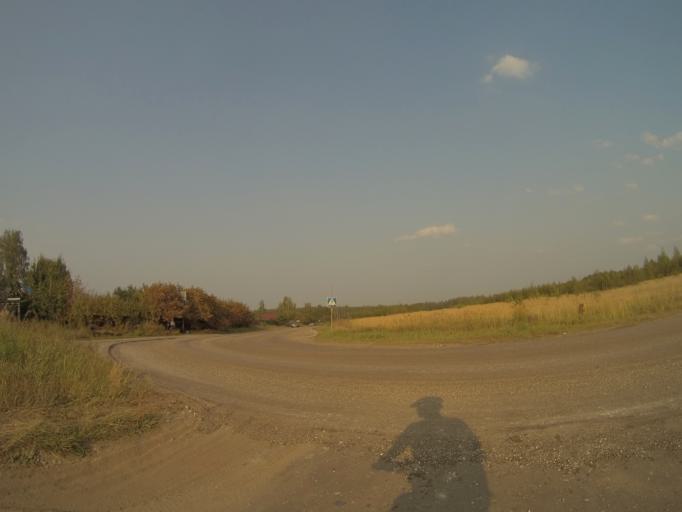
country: RU
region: Vladimir
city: Orgtrud
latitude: 56.2046
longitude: 40.5859
